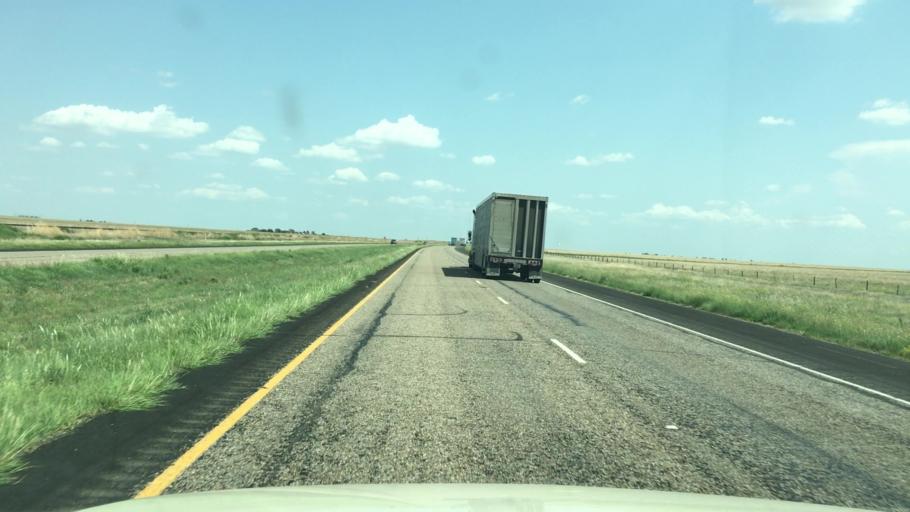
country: US
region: Texas
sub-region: Armstrong County
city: Claude
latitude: 35.1272
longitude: -101.4026
